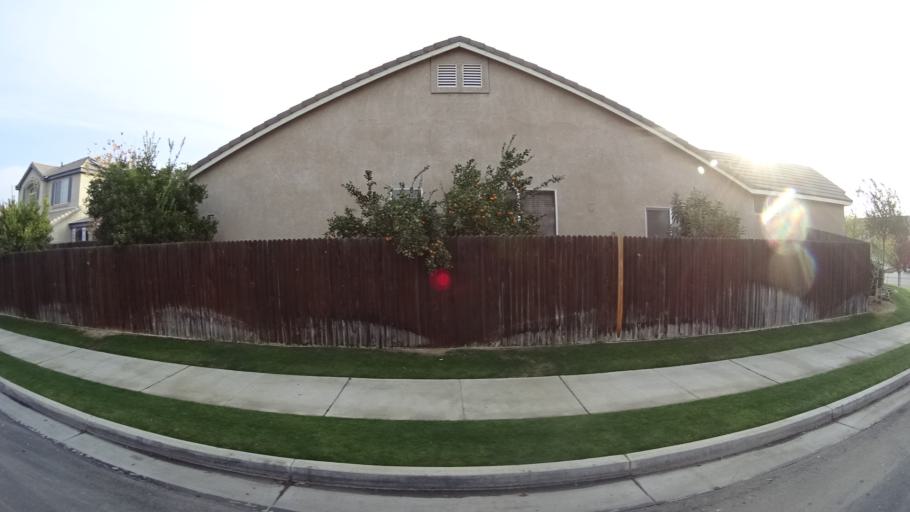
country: US
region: California
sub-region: Kern County
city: Greenacres
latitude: 35.4250
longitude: -119.1249
